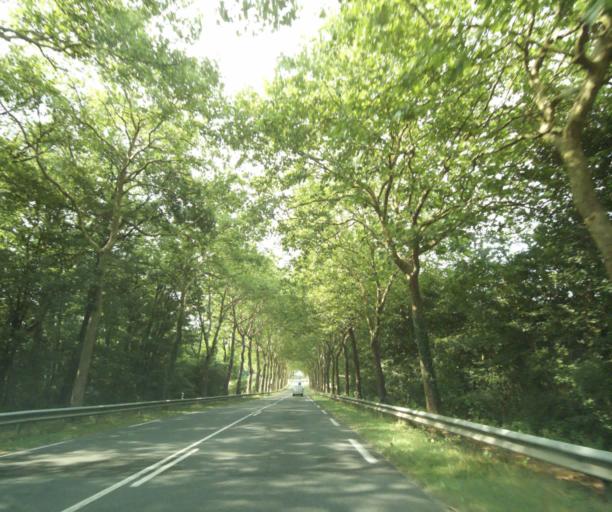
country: FR
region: Centre
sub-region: Departement d'Indre-et-Loire
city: La Membrolle-sur-Choisille
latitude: 47.4513
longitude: 0.6295
